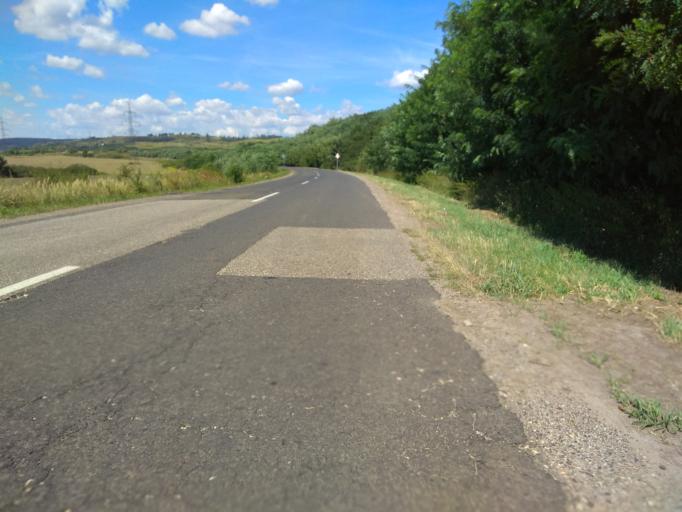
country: HU
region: Borsod-Abauj-Zemplen
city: Sajokaza
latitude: 48.2858
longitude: 20.6198
